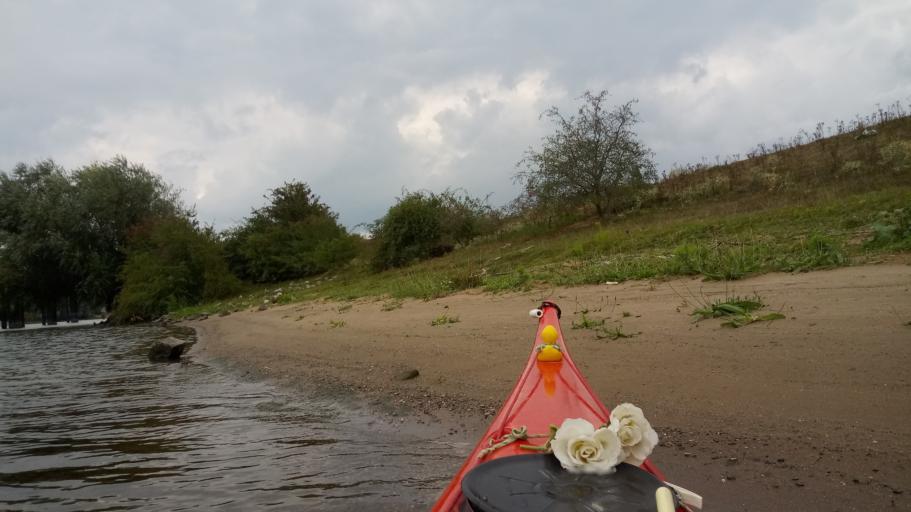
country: NL
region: Gelderland
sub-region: Gemeente Maasdriel
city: Heerewaarden
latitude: 51.7956
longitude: 5.3584
